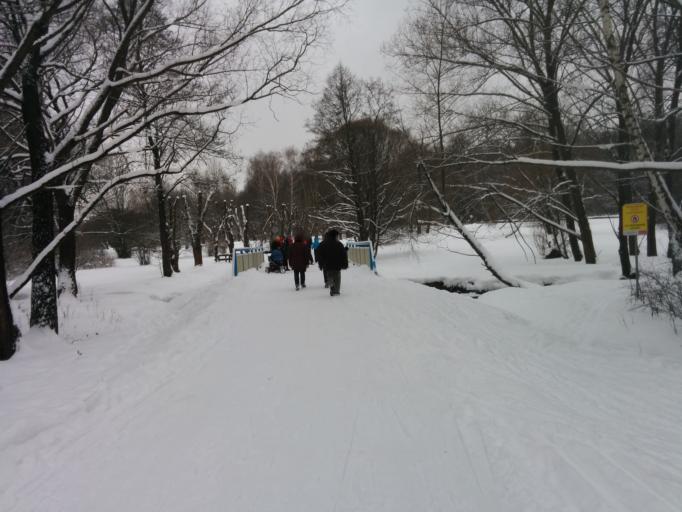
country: RU
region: Moskovskaya
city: Izmaylovo
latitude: 55.7831
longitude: 37.7796
